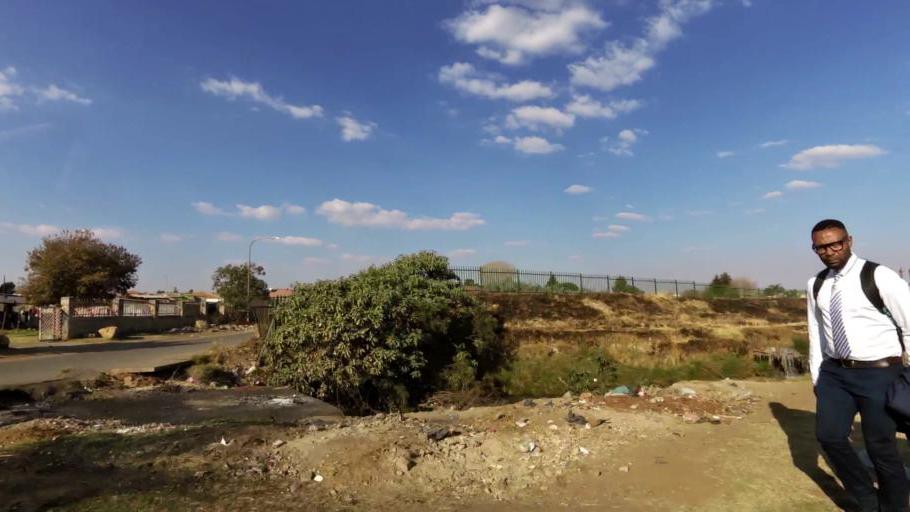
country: ZA
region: Gauteng
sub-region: City of Johannesburg Metropolitan Municipality
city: Soweto
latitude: -26.2171
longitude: 27.8768
